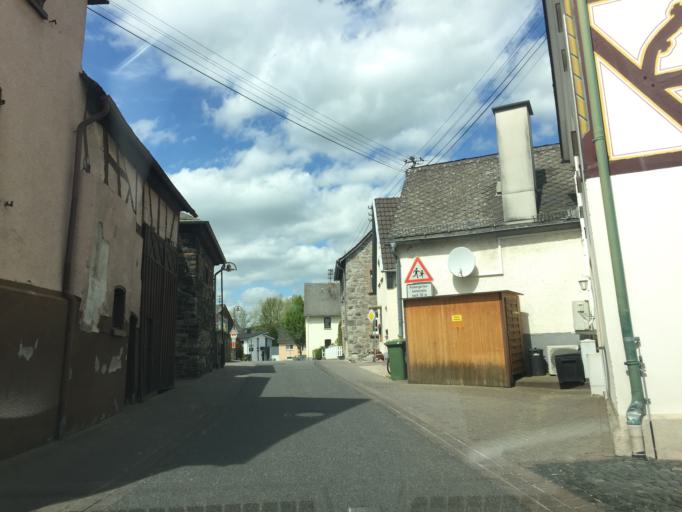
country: DE
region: Rheinland-Pfalz
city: Meudt
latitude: 50.4936
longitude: 7.8967
